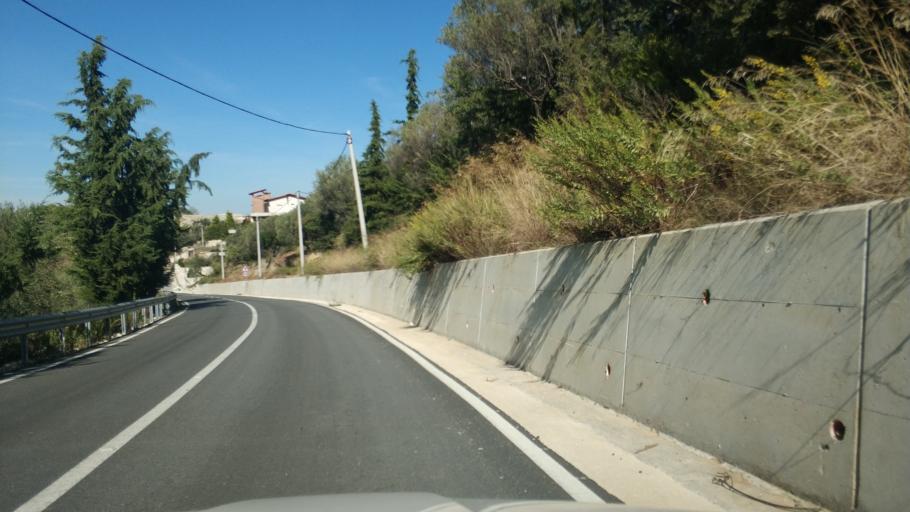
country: AL
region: Vlore
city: Vlore
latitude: 40.4544
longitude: 19.5153
